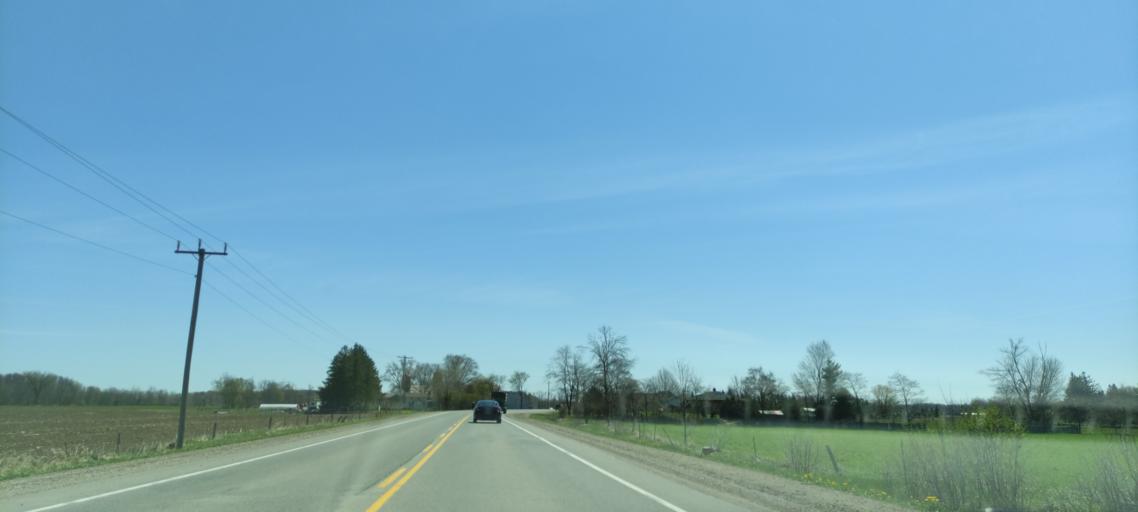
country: CA
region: Ontario
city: Waterloo
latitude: 43.5812
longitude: -80.4203
